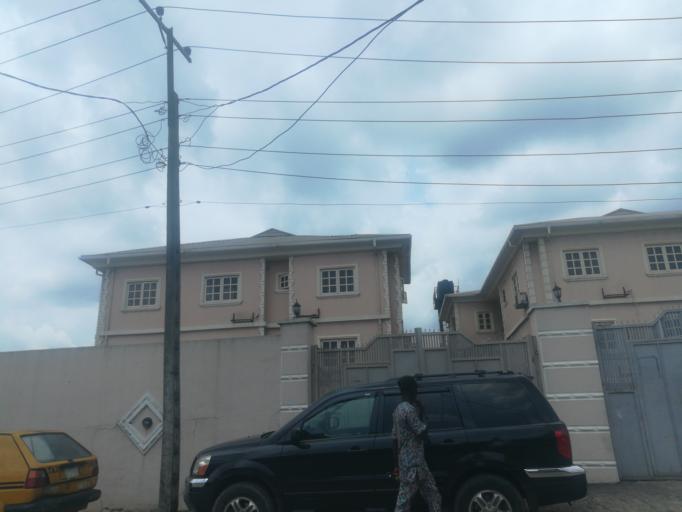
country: NG
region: Lagos
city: Somolu
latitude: 6.5601
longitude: 3.3859
